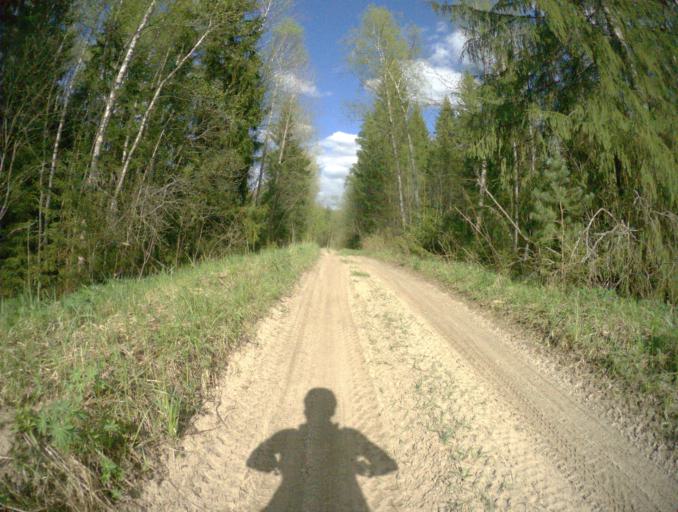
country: RU
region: Vladimir
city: Golovino
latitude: 55.8953
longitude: 40.4190
